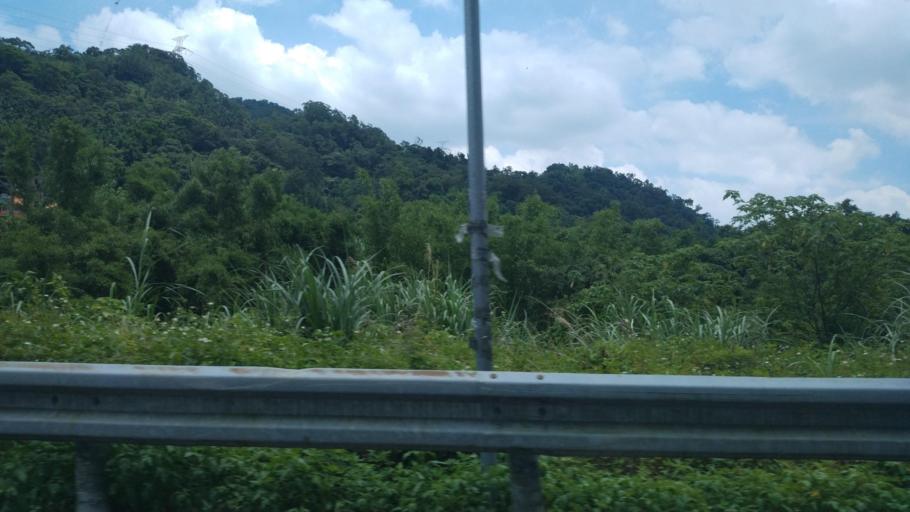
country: TW
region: Taipei
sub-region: Taipei
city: Banqiao
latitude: 24.9274
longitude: 121.4475
